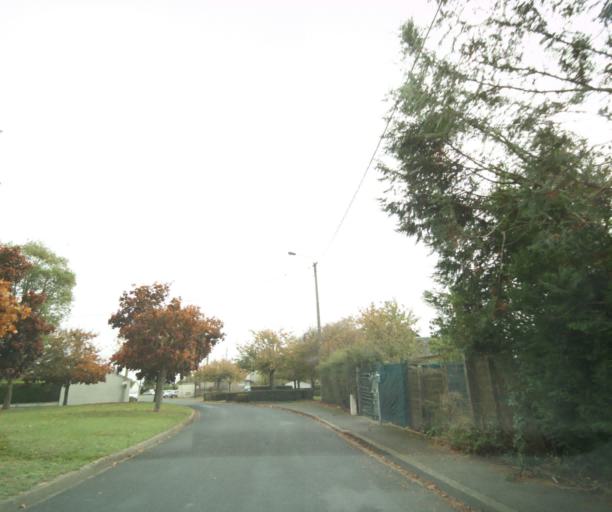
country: FR
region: Centre
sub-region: Departement d'Eure-et-Loir
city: Dreux
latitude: 48.7467
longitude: 1.3395
